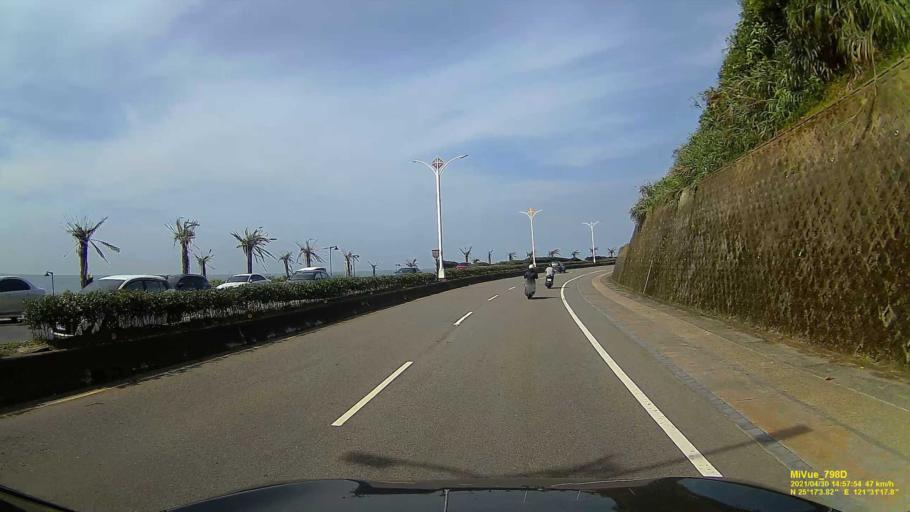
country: TW
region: Taipei
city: Taipei
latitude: 25.2846
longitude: 121.5218
